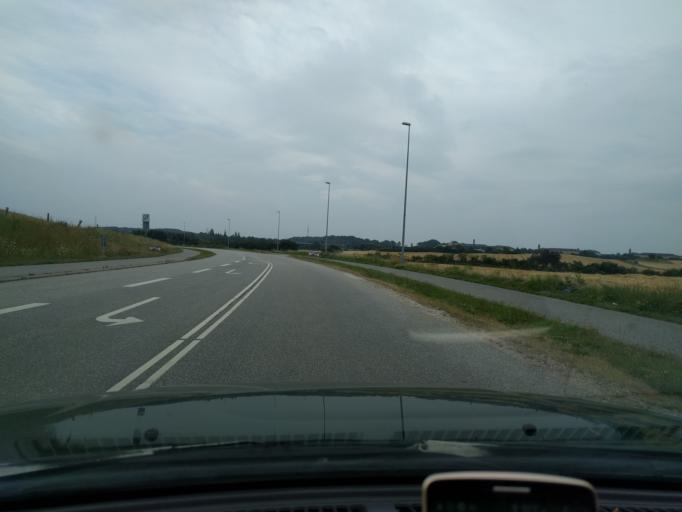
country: DK
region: Zealand
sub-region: Slagelse Kommune
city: Korsor
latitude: 55.3565
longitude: 11.1375
